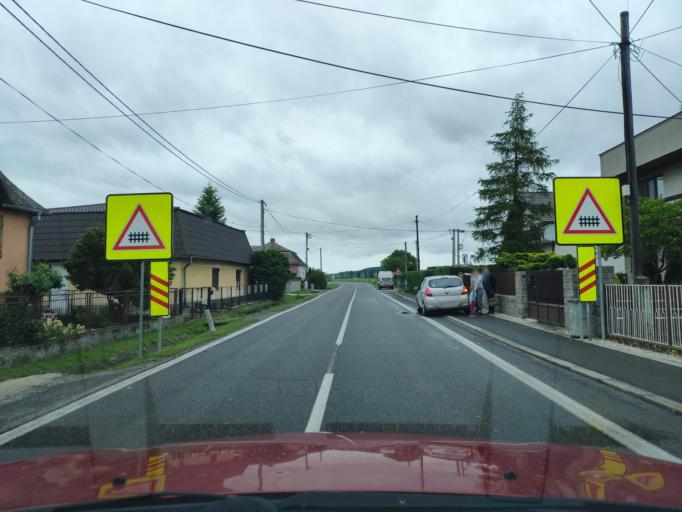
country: HU
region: Borsod-Abauj-Zemplen
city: Satoraljaujhely
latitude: 48.4104
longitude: 21.6679
